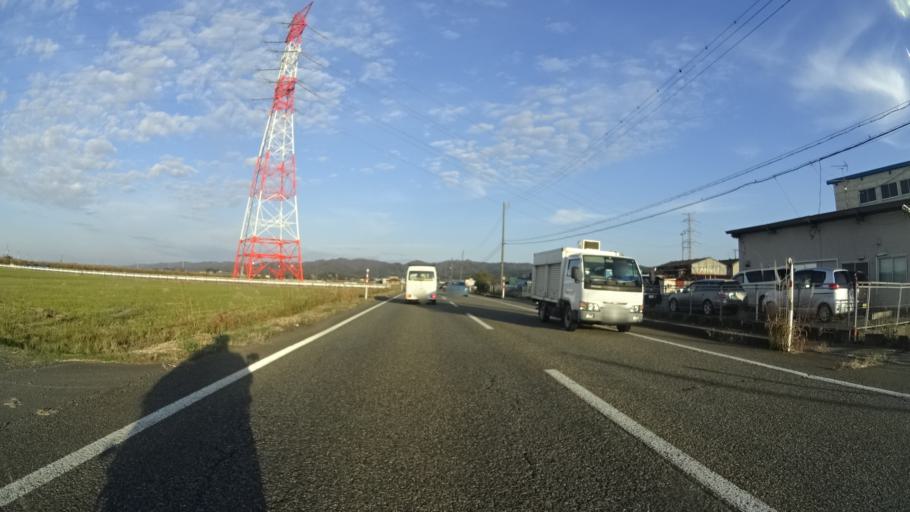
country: JP
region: Niigata
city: Kashiwazaki
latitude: 37.3998
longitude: 138.6159
